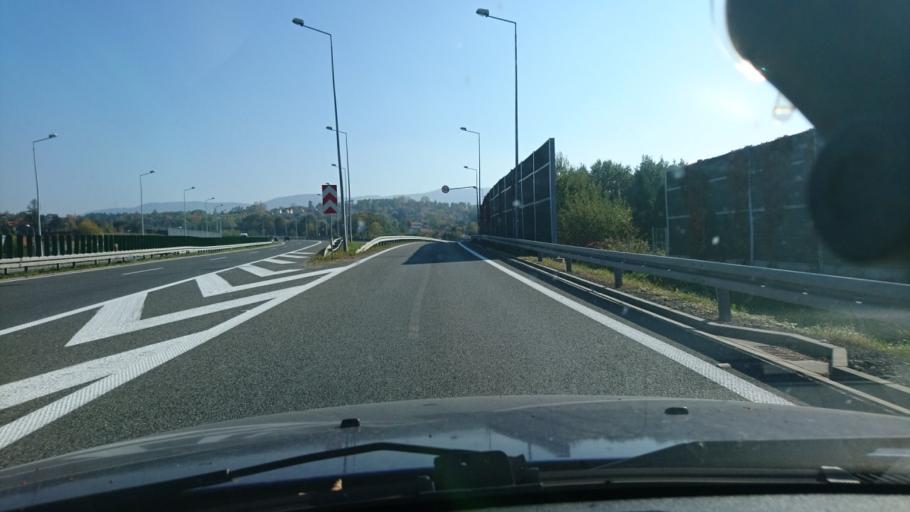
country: PL
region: Silesian Voivodeship
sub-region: Bielsko-Biala
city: Bielsko-Biala
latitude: 49.8455
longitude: 19.0661
